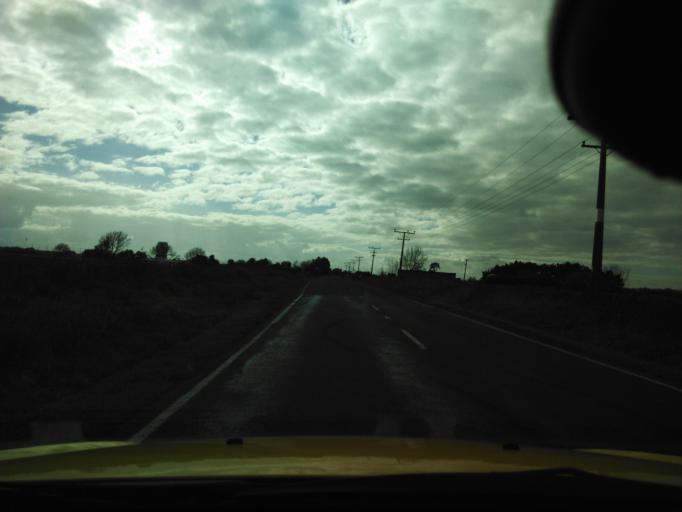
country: NZ
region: Waikato
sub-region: Waikato District
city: Te Kauwhata
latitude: -37.4722
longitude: 175.1452
